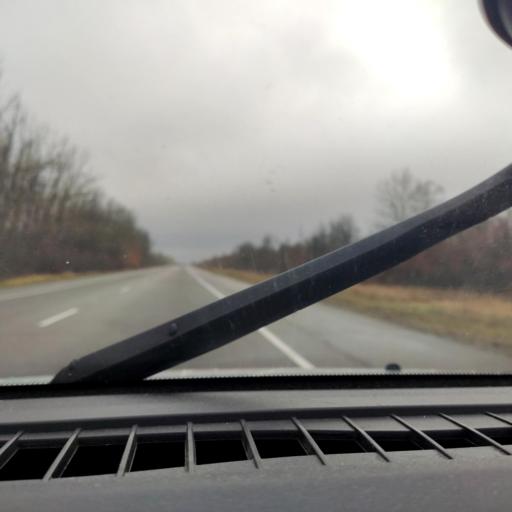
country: RU
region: Voronezj
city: Kolodeznyy
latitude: 51.2739
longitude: 39.0469
